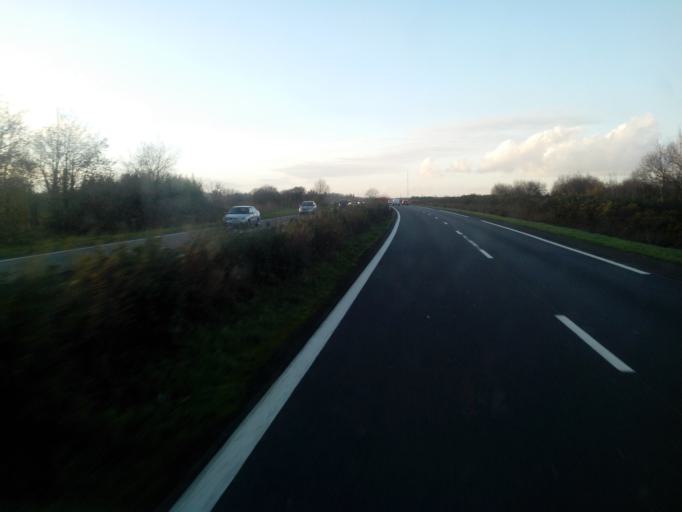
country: FR
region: Pays de la Loire
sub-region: Departement de la Loire-Atlantique
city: La Haie-Fouassiere
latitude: 47.1703
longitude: -1.3801
